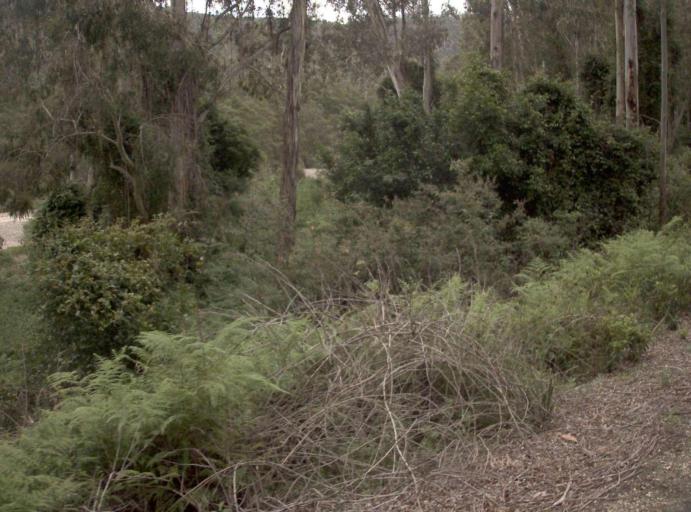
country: AU
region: New South Wales
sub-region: Bombala
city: Bombala
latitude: -37.4638
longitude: 149.1859
